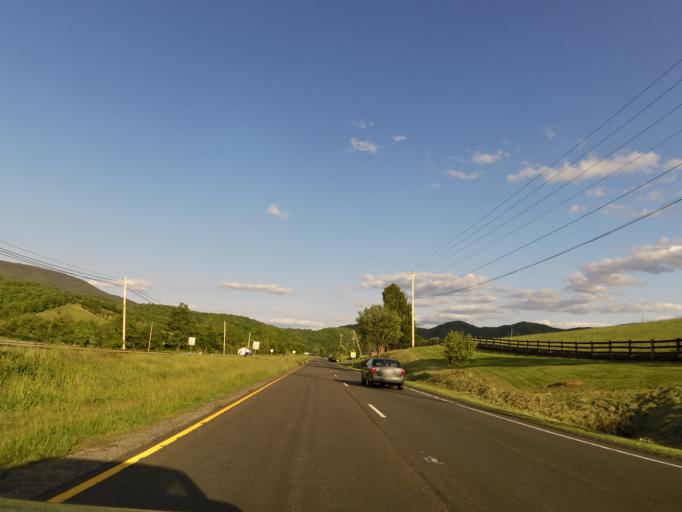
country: US
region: Virginia
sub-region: Russell County
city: Lebanon
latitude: 36.8220
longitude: -82.1388
